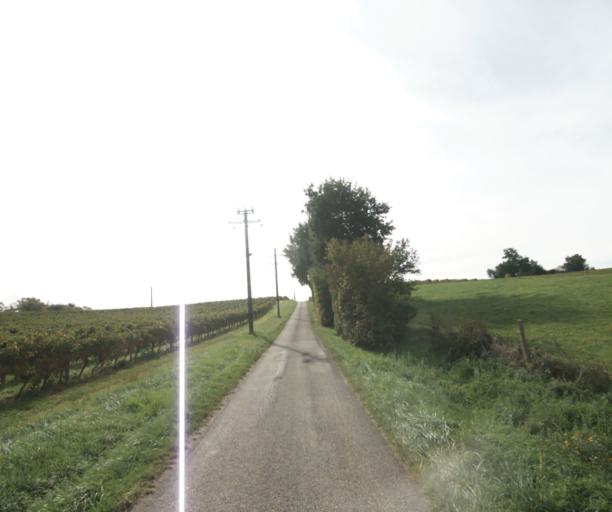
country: FR
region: Midi-Pyrenees
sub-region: Departement du Gers
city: Eauze
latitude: 43.8756
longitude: 0.1401
